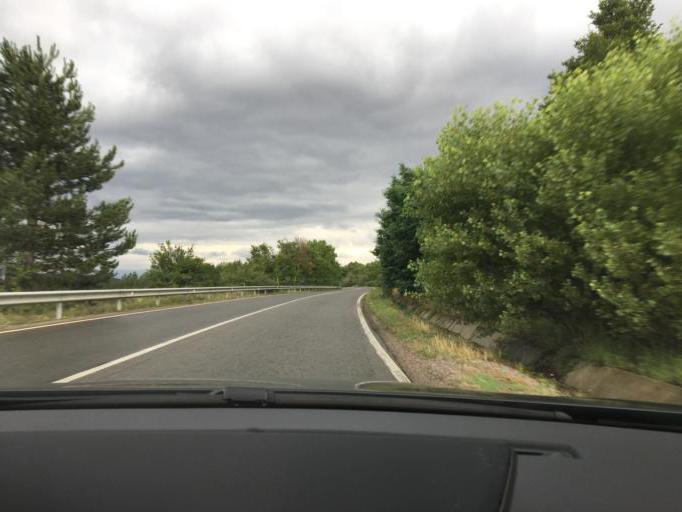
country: BG
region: Kyustendil
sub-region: Obshtina Boboshevo
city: Boboshevo
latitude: 42.2480
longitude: 22.8949
